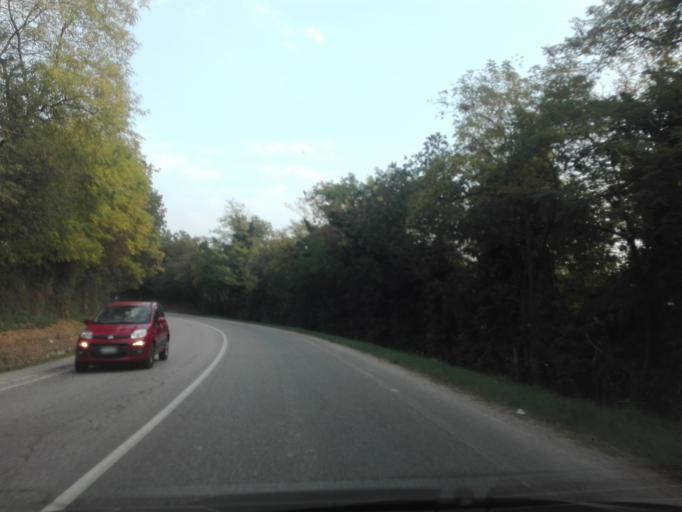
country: IT
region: Veneto
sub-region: Provincia di Verona
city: Lazise
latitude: 45.4924
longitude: 10.7572
